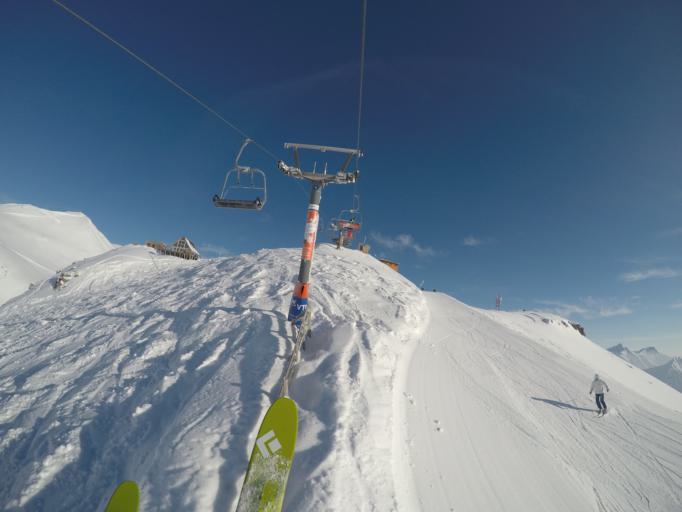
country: GE
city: Gudauri
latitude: 42.4964
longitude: 44.5071
